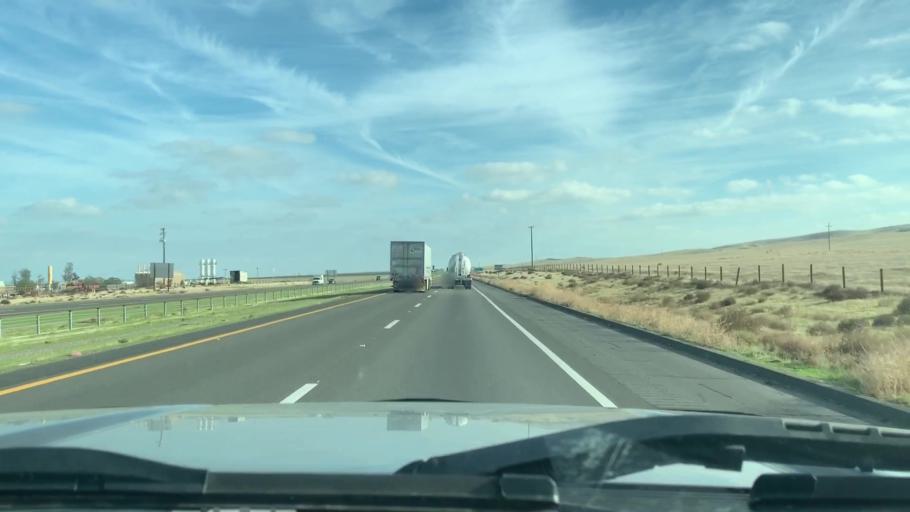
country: US
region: California
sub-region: Kings County
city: Avenal
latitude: 36.0721
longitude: -120.0947
